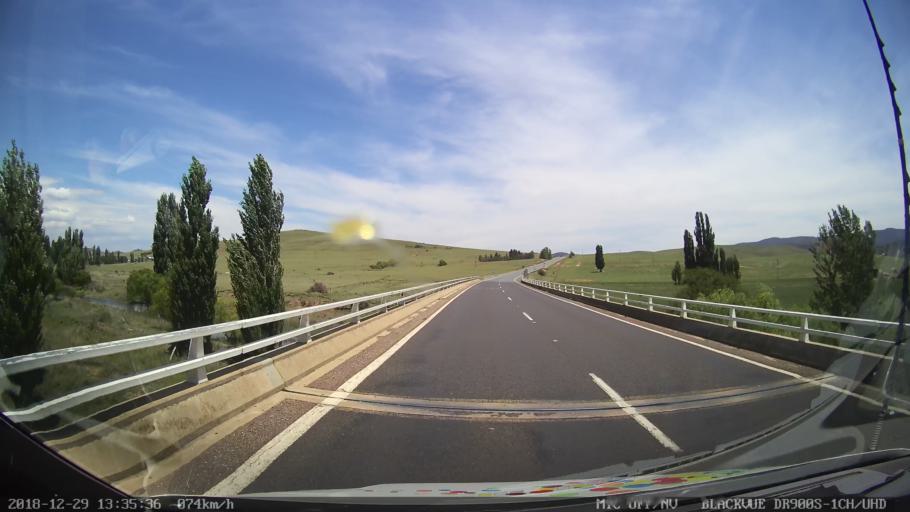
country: AU
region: New South Wales
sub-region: Cooma-Monaro
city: Cooma
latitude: -35.9609
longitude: 149.1486
